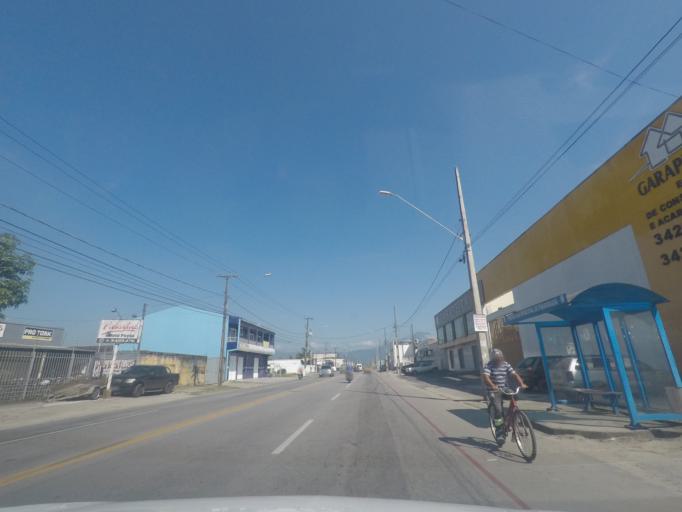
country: BR
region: Parana
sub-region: Paranagua
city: Paranagua
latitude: -25.5539
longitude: -48.5527
